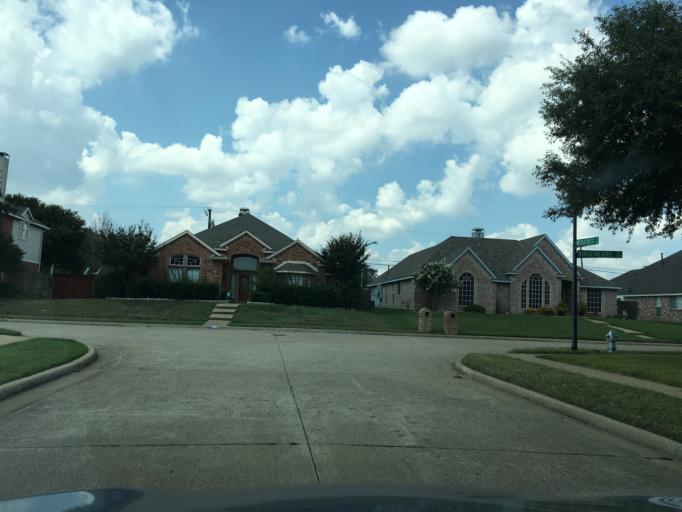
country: US
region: Texas
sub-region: Dallas County
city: Garland
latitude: 32.9403
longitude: -96.6467
